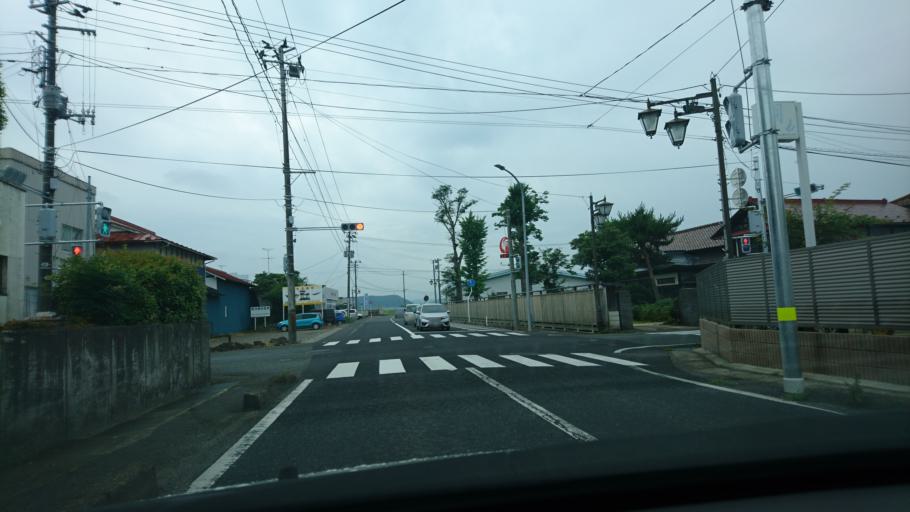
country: JP
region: Miyagi
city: Furukawa
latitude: 38.7348
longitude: 140.9550
